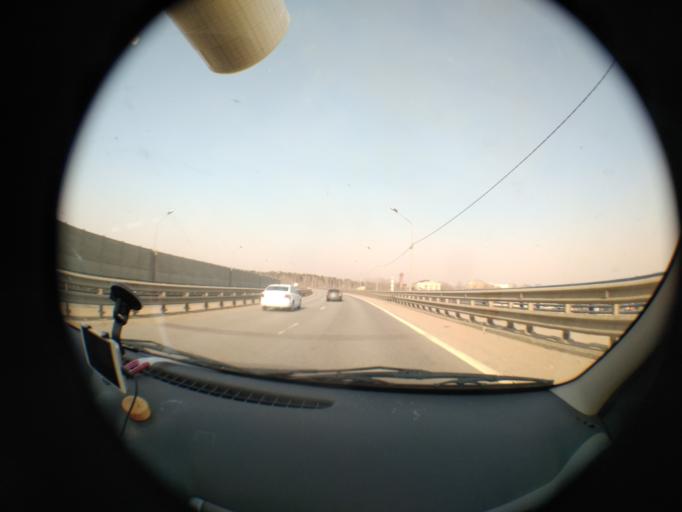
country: RU
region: Moskovskaya
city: Zhukovskiy
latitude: 55.5730
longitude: 38.1126
